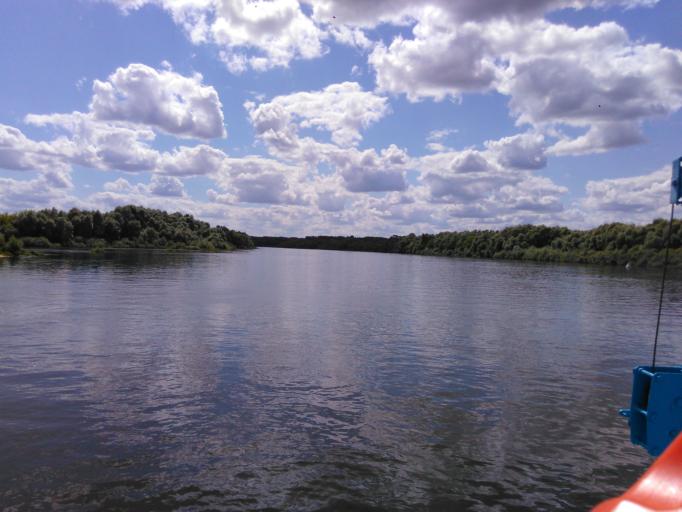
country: RU
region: Rjazan
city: Polyany
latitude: 54.6614
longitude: 39.7914
